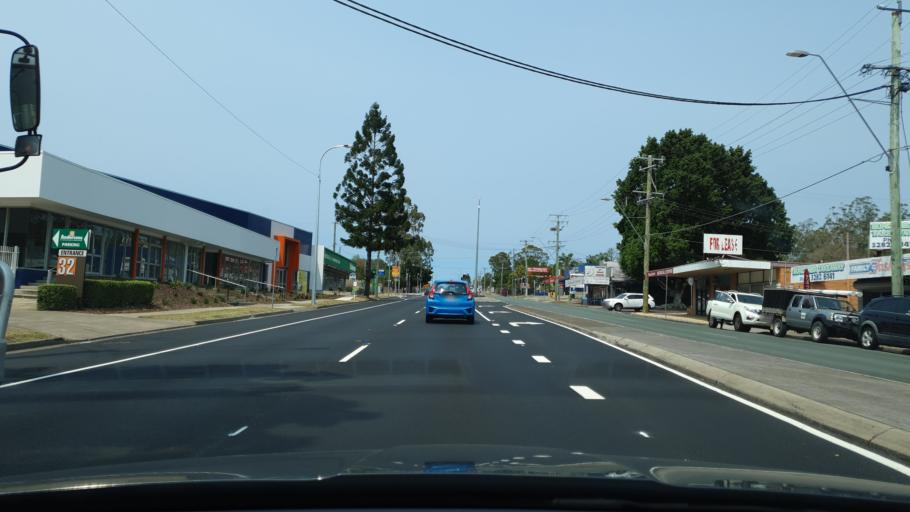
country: AU
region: Queensland
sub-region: Ipswich
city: Bundamba
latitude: -27.6085
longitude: 152.8108
